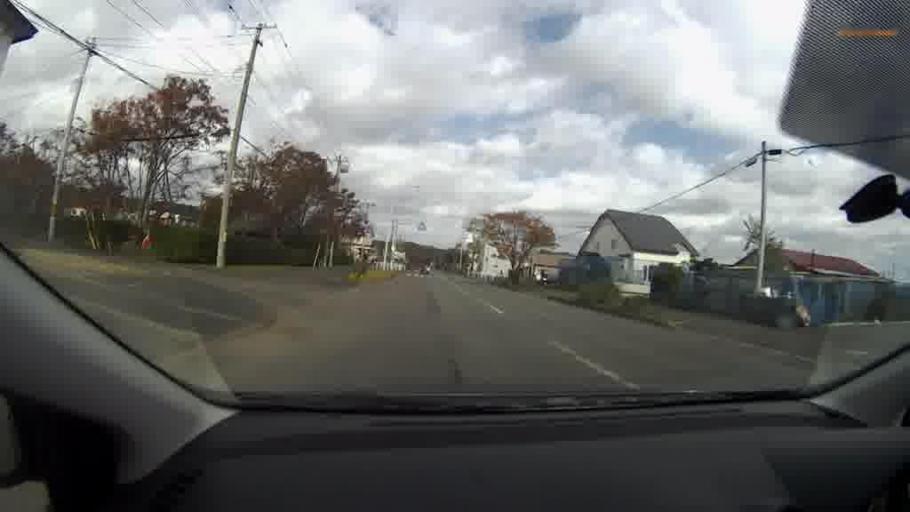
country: JP
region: Hokkaido
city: Kushiro
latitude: 42.9794
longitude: 144.1275
